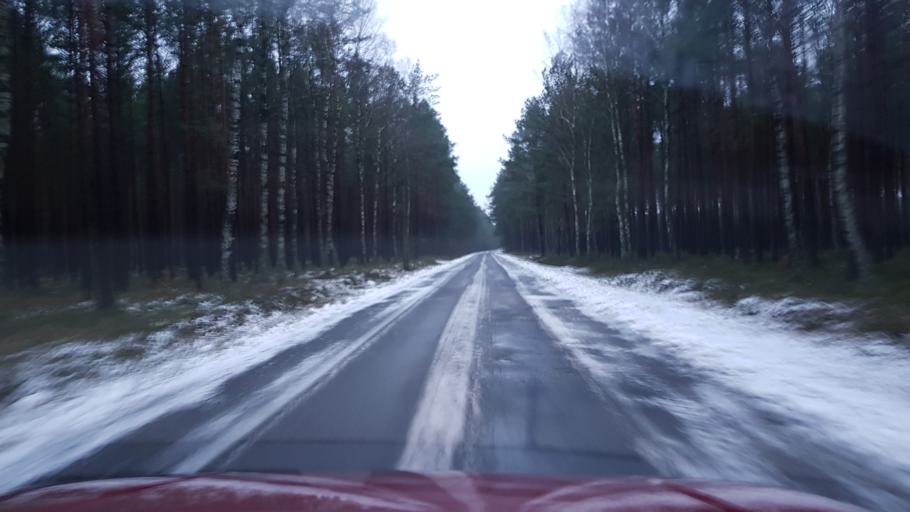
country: PL
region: West Pomeranian Voivodeship
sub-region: Powiat goleniowski
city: Goleniow
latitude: 53.4870
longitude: 14.8562
